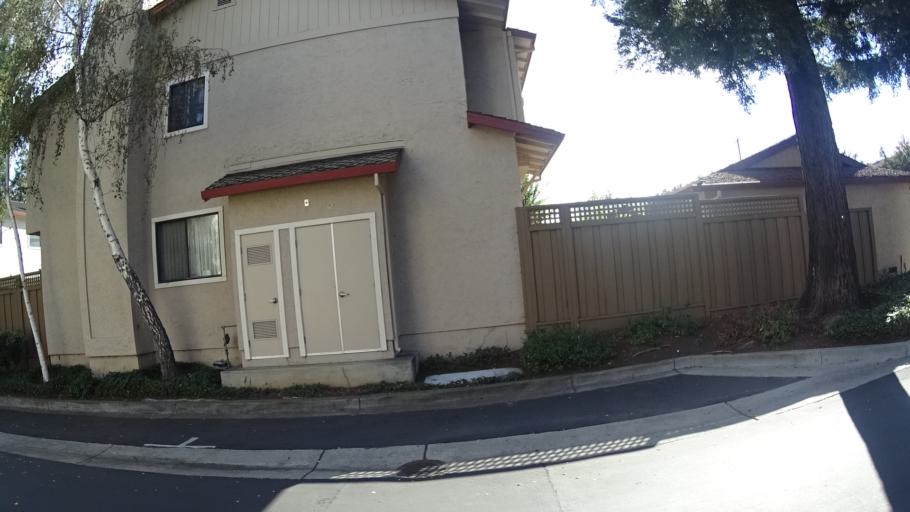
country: US
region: California
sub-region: Santa Clara County
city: Santa Clara
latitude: 37.3596
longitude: -121.9629
